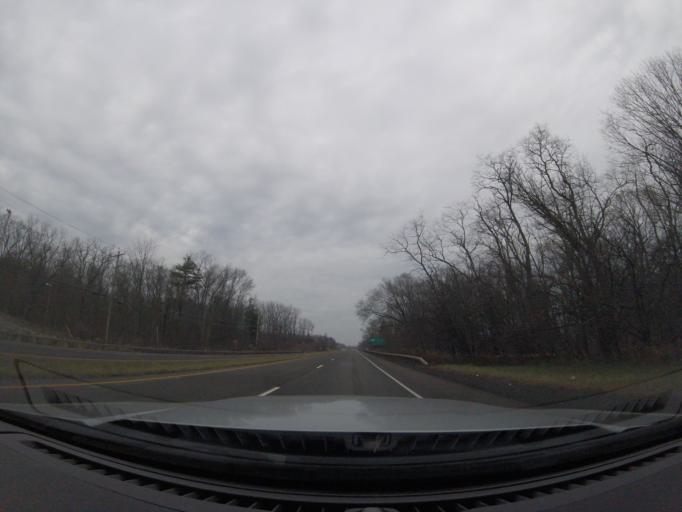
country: US
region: New York
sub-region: Schuyler County
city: Watkins Glen
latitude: 42.4126
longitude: -76.9006
